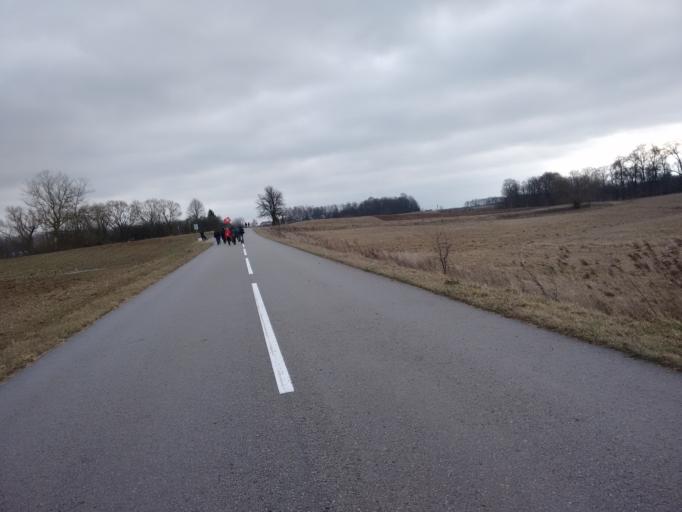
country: LT
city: Veisiejai
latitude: 54.2449
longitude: 23.8702
